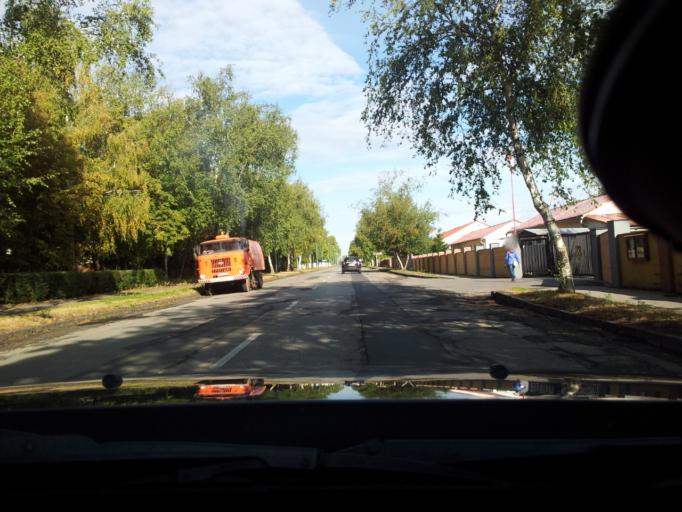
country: SK
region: Kosicky
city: Michalovce
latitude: 48.7640
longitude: 21.9064
